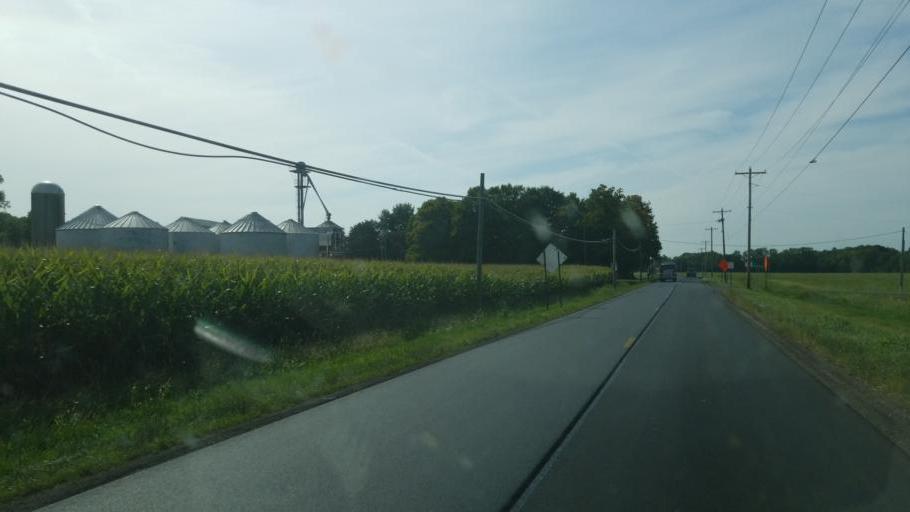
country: US
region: Ohio
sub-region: Knox County
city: Mount Vernon
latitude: 40.3984
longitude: -82.5305
